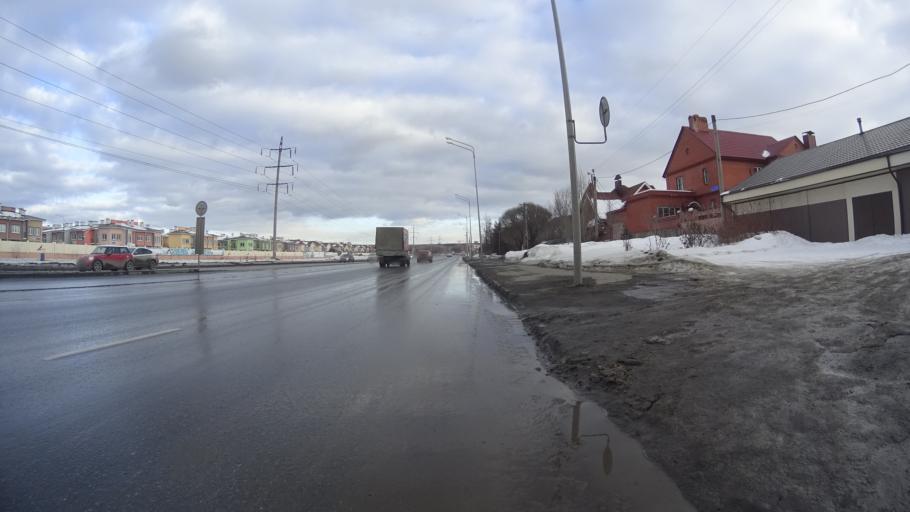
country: RU
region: Chelyabinsk
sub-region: Gorod Chelyabinsk
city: Chelyabinsk
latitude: 55.1559
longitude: 61.3101
